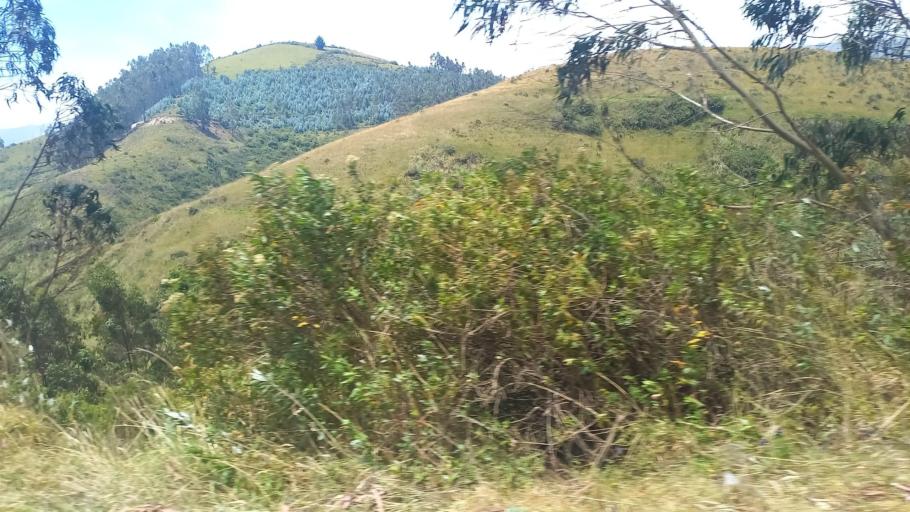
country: EC
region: Pichincha
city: Cayambe
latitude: 0.1792
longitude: -78.0919
